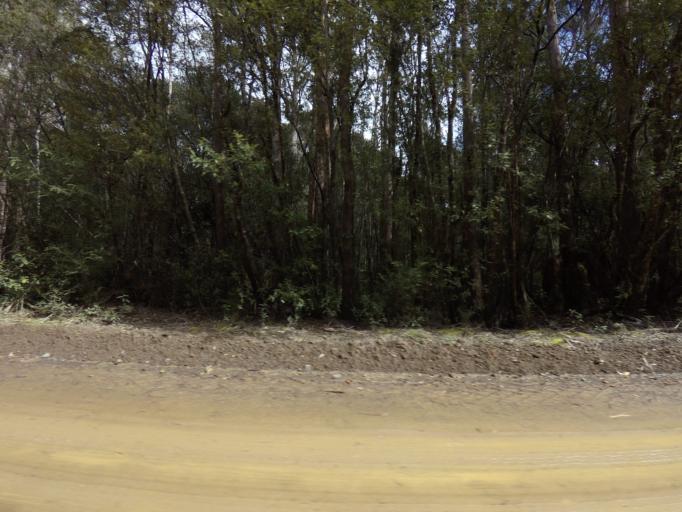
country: AU
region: Tasmania
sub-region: Huon Valley
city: Geeveston
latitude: -43.4101
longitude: 146.8723
